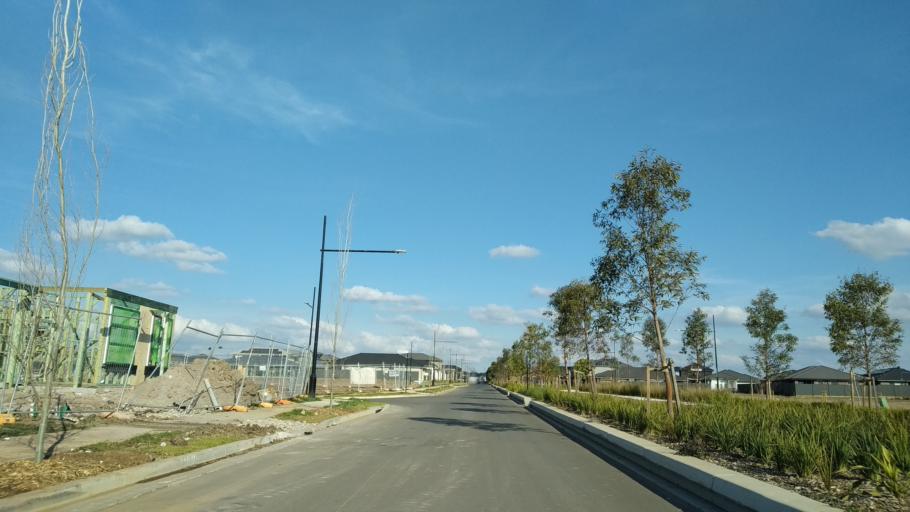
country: AU
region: New South Wales
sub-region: Blacktown
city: Blackett
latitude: -33.6900
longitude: 150.8147
